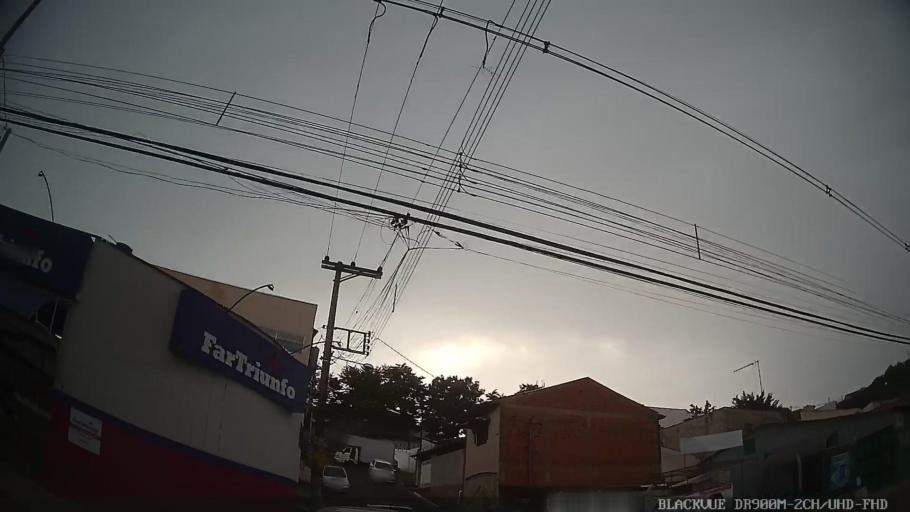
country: BR
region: Sao Paulo
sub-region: Pedreira
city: Pedreira
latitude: -22.7182
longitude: -46.8928
